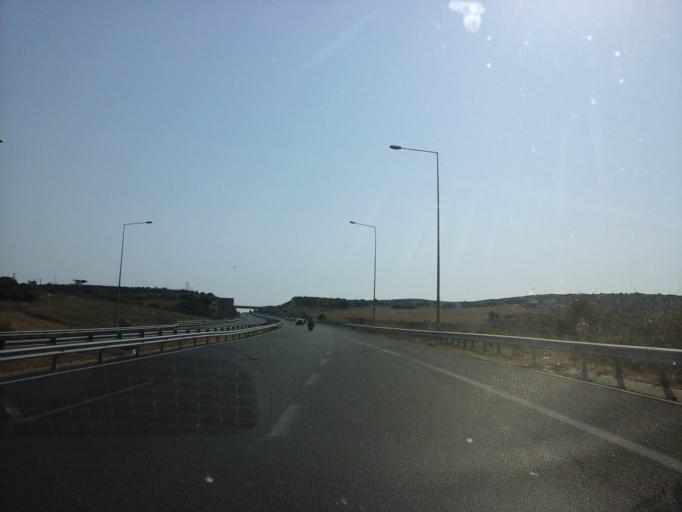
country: GR
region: East Macedonia and Thrace
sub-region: Nomos Evrou
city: Alexandroupoli
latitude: 40.8771
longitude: 25.8524
